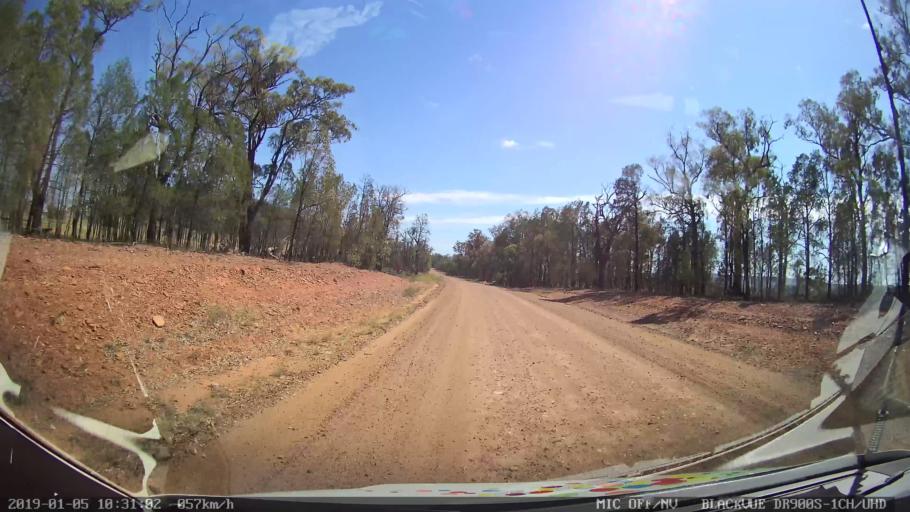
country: AU
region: New South Wales
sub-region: Gilgandra
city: Gilgandra
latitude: -31.5275
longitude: 148.9265
